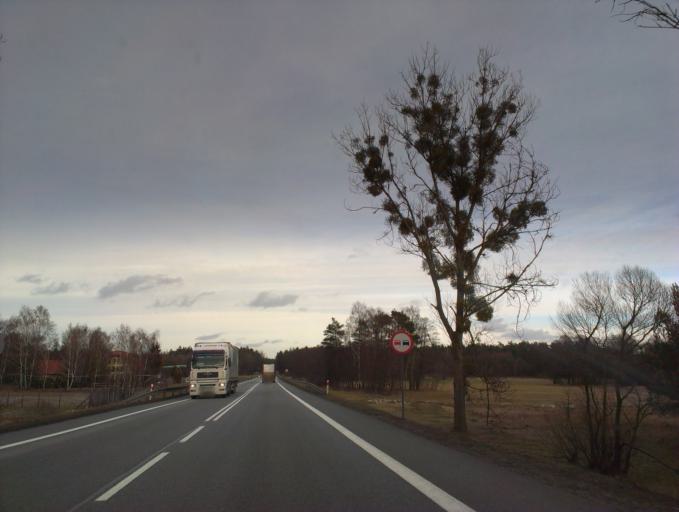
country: PL
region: Kujawsko-Pomorskie
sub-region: Powiat lipnowski
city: Skepe
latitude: 52.8807
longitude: 19.3812
